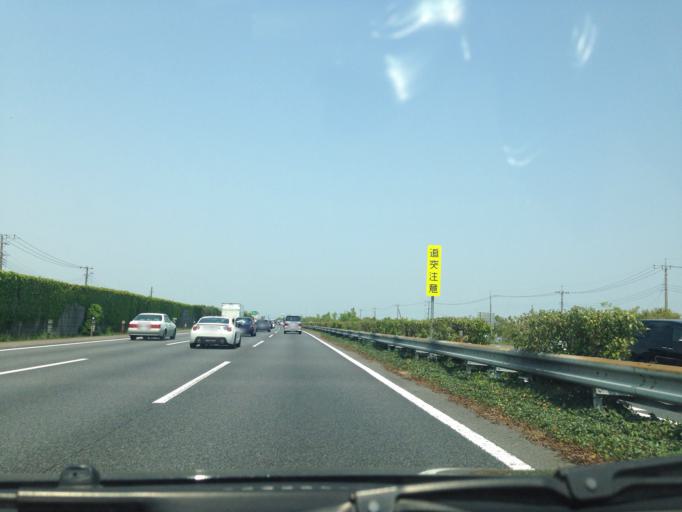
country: JP
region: Saitama
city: Hanyu
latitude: 36.1947
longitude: 139.5817
